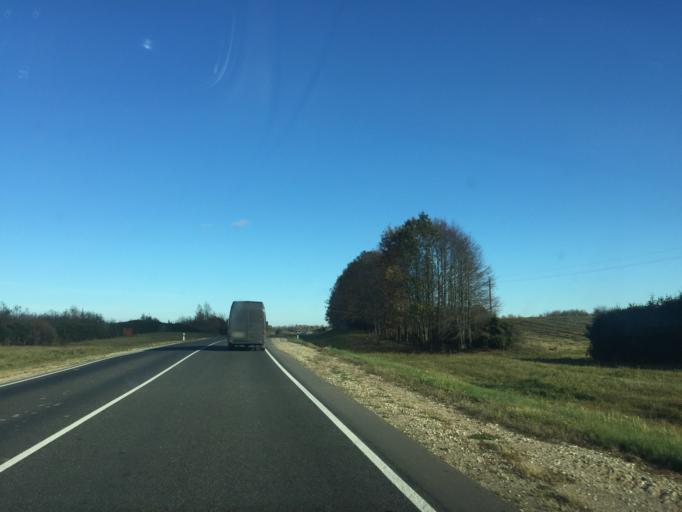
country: BY
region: Vitebsk
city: Dzisna
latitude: 55.3028
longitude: 28.2276
